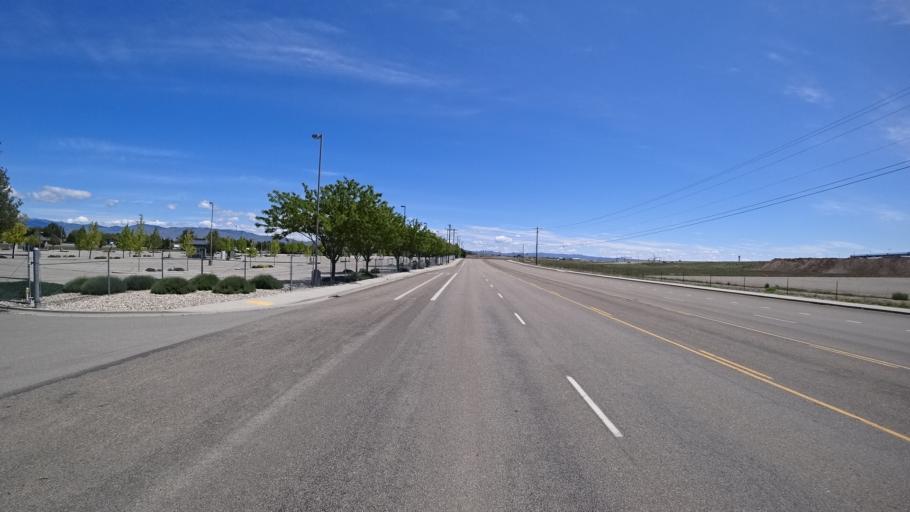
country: US
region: Idaho
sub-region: Ada County
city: Garden City
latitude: 43.5754
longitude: -116.2510
